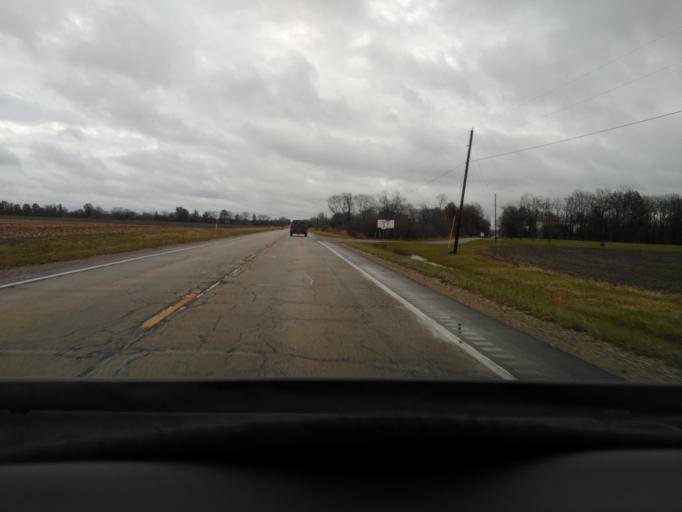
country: US
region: Illinois
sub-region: Effingham County
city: Altamont
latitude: 39.0438
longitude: -88.7844
